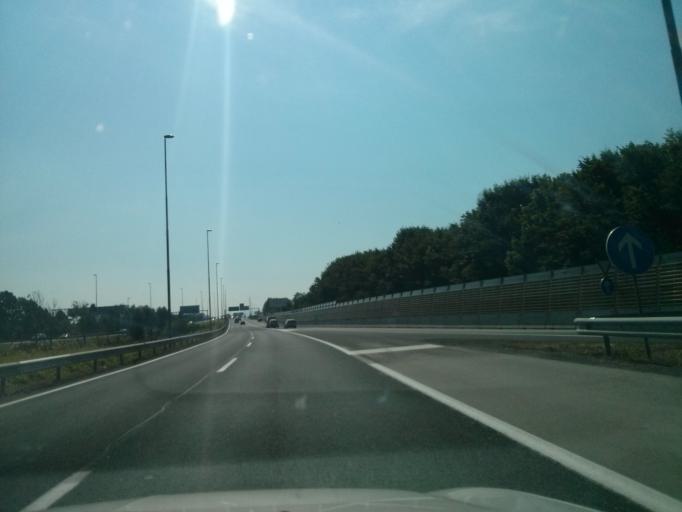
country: SI
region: Brezovica
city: Vnanje Gorice
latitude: 46.0372
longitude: 14.4540
